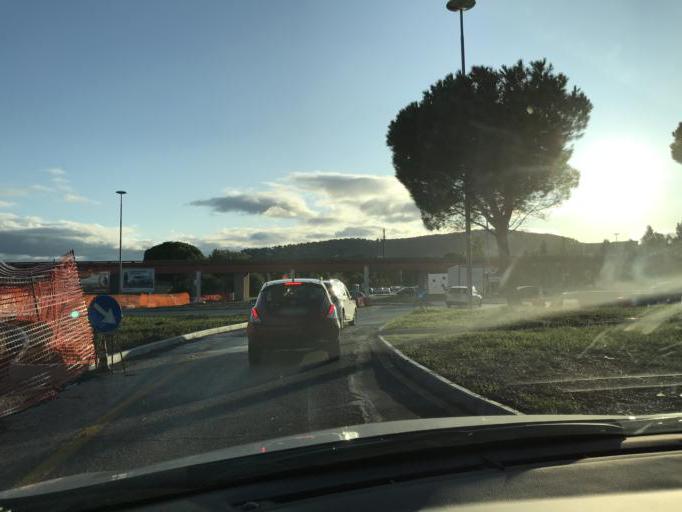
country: IT
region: Umbria
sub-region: Provincia di Perugia
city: Perugia
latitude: 43.1081
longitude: 12.3634
